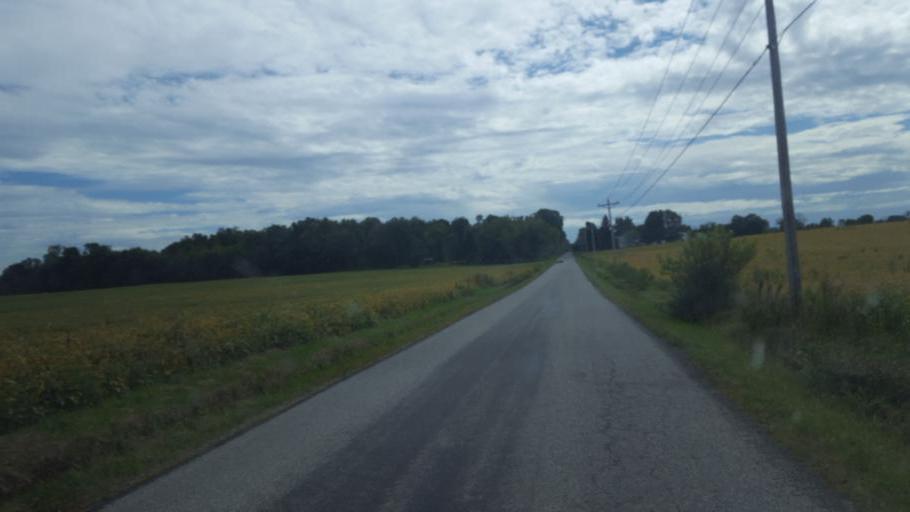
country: US
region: Ohio
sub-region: Licking County
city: Johnstown
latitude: 40.1525
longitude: -82.7203
